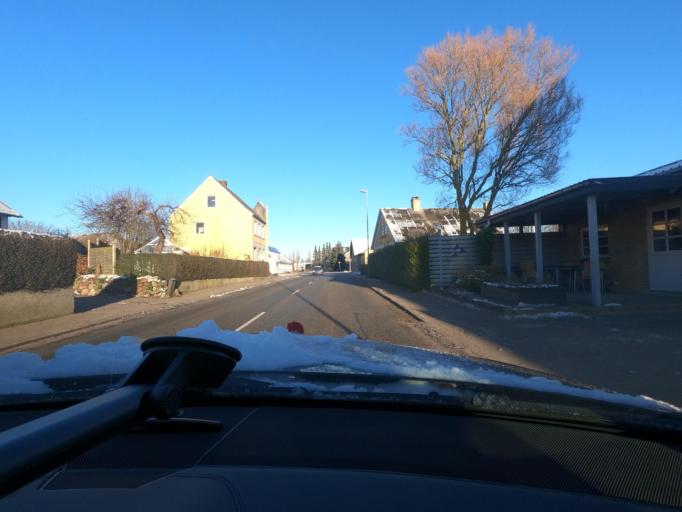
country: DK
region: South Denmark
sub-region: Sonderborg Kommune
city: Horuphav
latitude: 54.8812
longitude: 9.9953
